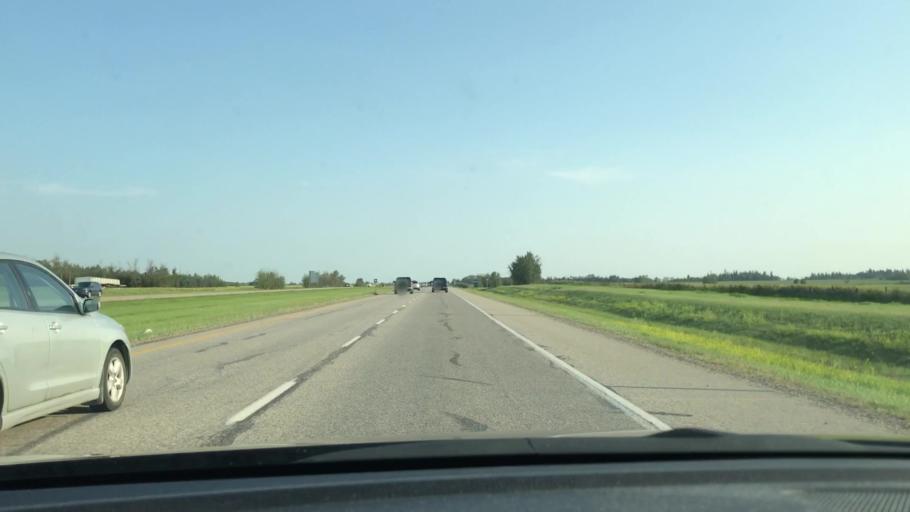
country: CA
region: Alberta
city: Millet
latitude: 53.0830
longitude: -113.5984
